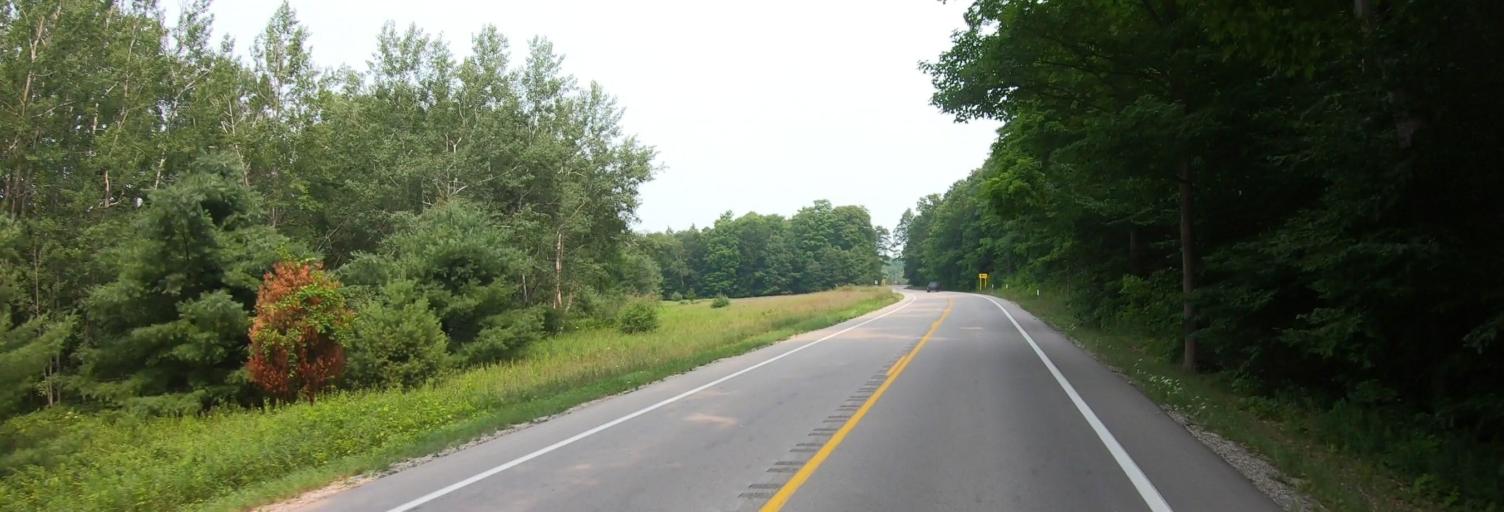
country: US
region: Michigan
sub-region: Leelanau County
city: Leland
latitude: 44.9296
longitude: -85.8170
